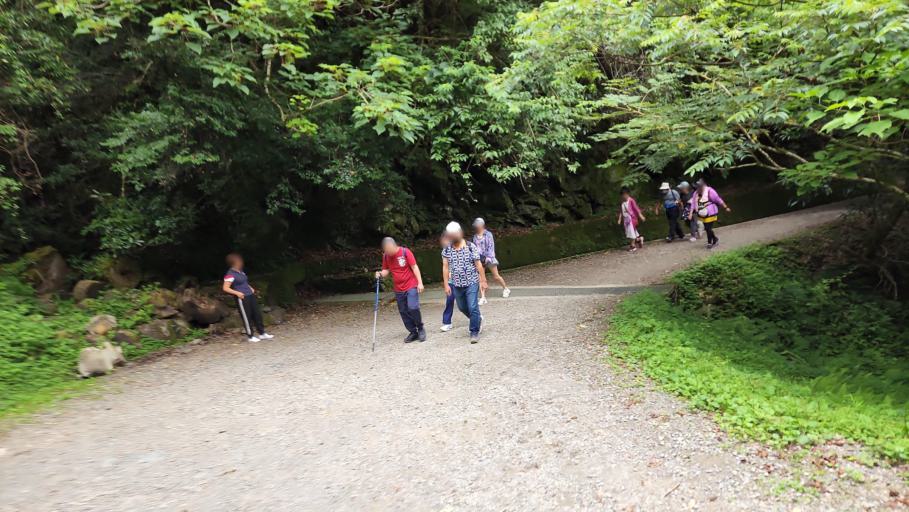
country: TW
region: Taiwan
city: Daxi
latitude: 24.7093
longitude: 121.4358
